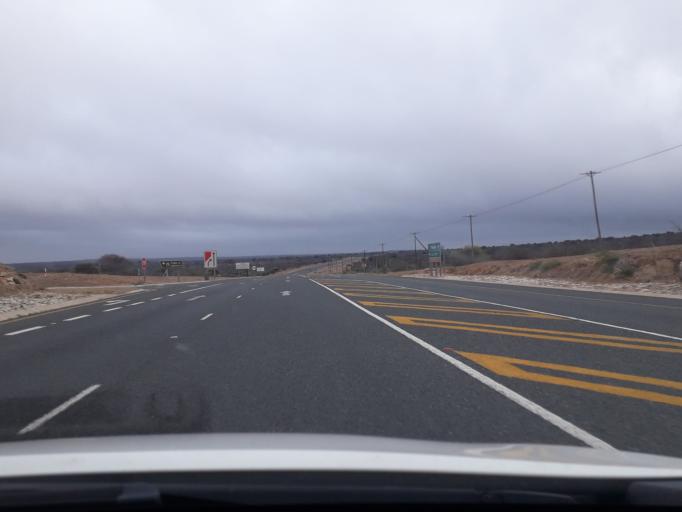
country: ZA
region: Limpopo
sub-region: Vhembe District Municipality
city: Louis Trichardt
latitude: -23.4351
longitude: 29.7473
